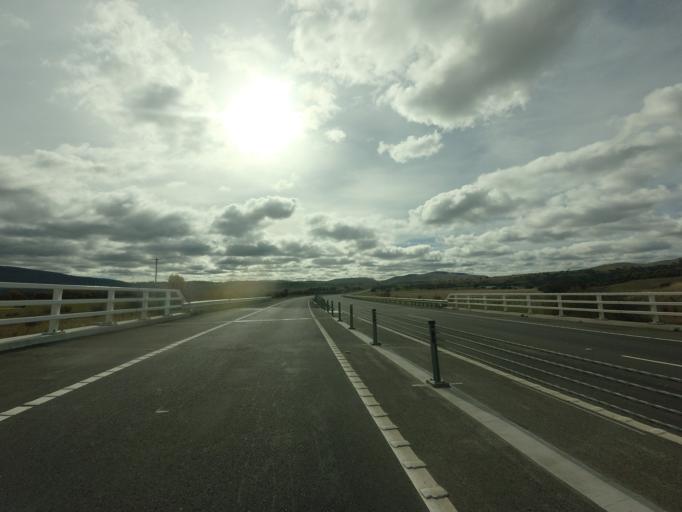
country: AU
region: Tasmania
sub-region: Brighton
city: Bridgewater
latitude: -42.4809
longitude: 147.1798
